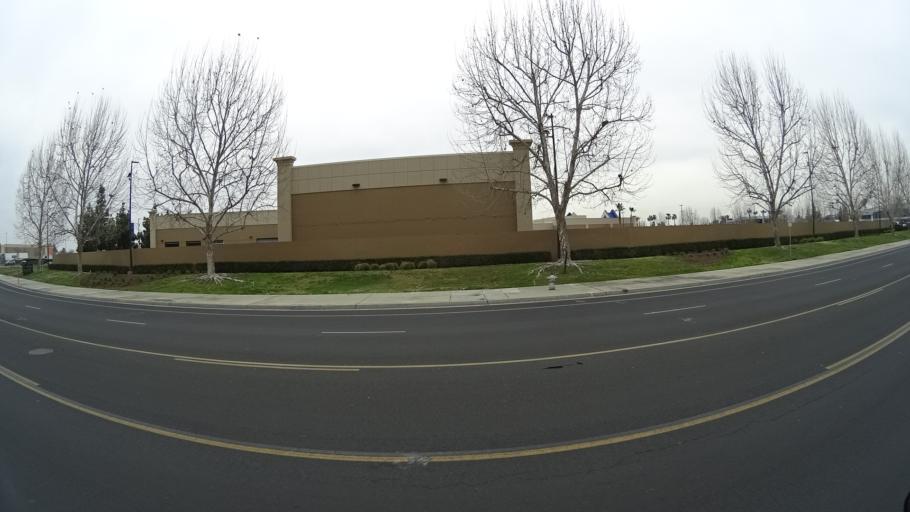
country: US
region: California
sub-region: Fresno County
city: Fresno
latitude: 36.8406
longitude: -119.8062
